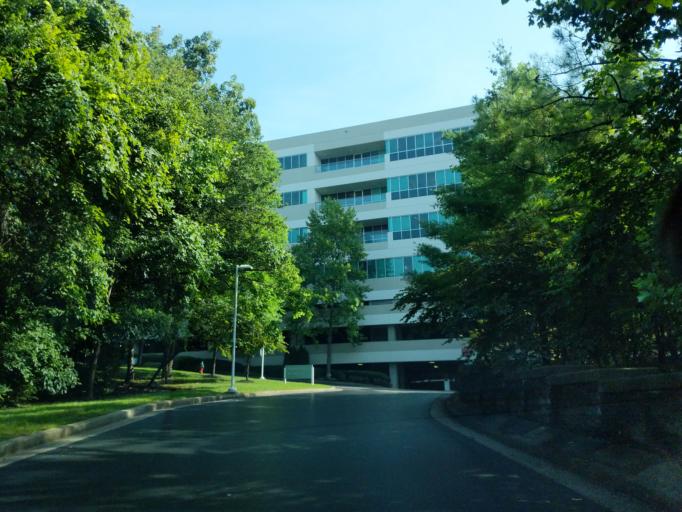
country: US
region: Tennessee
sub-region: Davidson County
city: Goodlettsville
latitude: 36.3085
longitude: -86.6997
